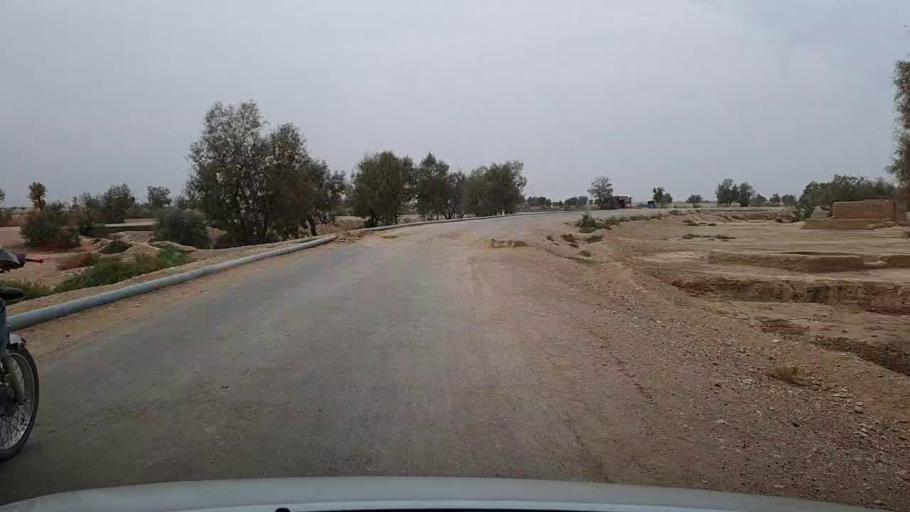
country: PK
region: Sindh
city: Sehwan
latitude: 26.3223
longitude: 67.7278
